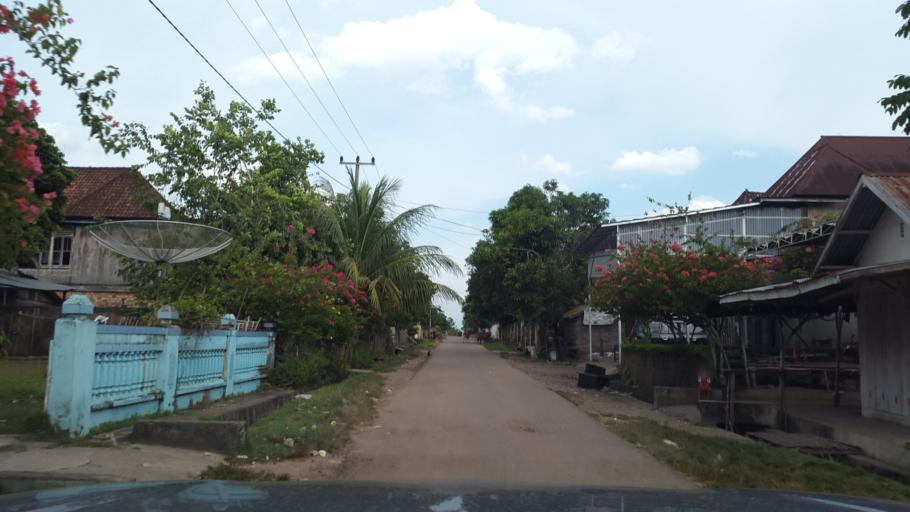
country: ID
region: South Sumatra
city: Glumbang
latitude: -3.4212
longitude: 104.4886
